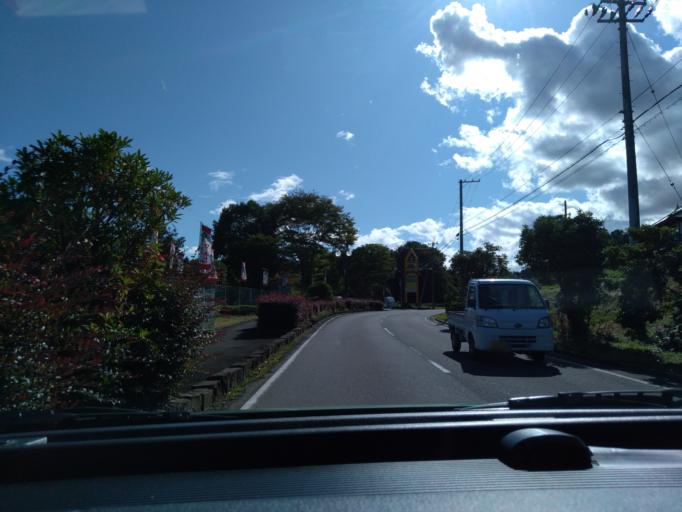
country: JP
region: Iwate
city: Ichinoseki
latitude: 38.7611
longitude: 141.1714
